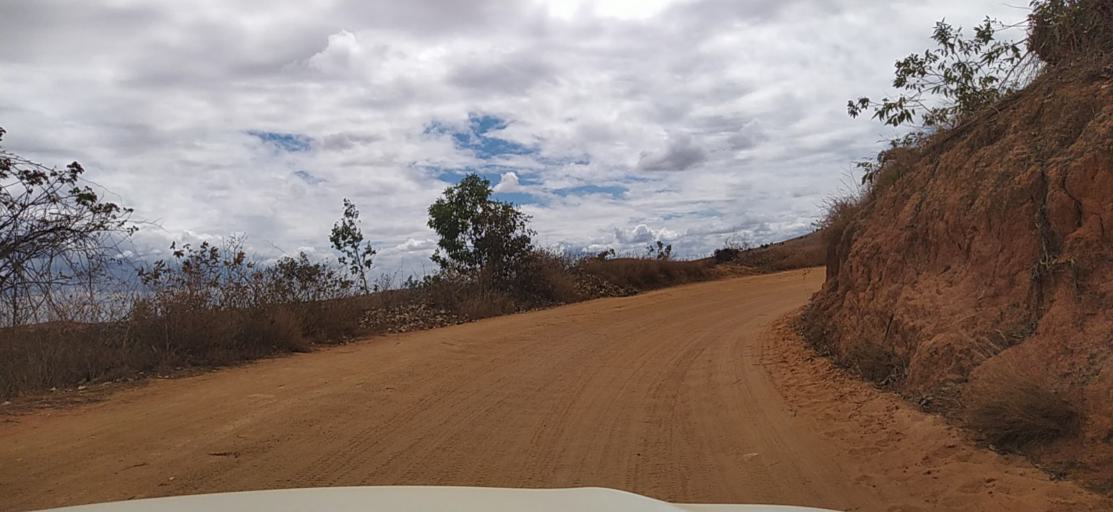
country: MG
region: Alaotra Mangoro
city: Ambatondrazaka
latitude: -17.9997
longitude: 48.2623
